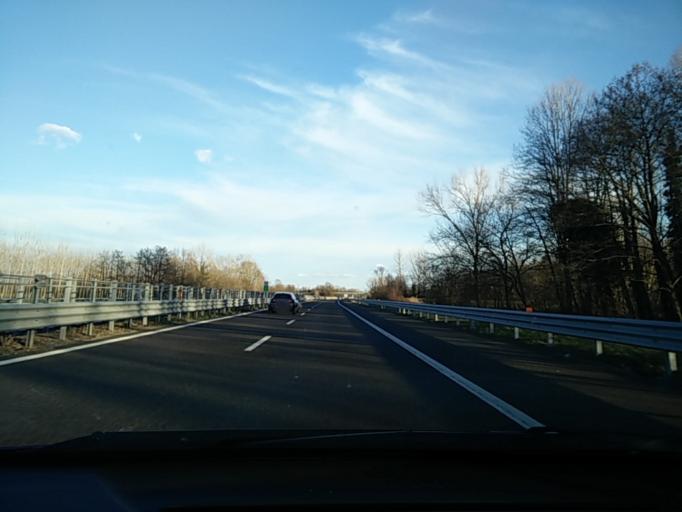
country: IT
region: Friuli Venezia Giulia
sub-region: Provincia di Udine
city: Collofedo di Monte Albano
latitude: 46.1822
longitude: 13.1289
